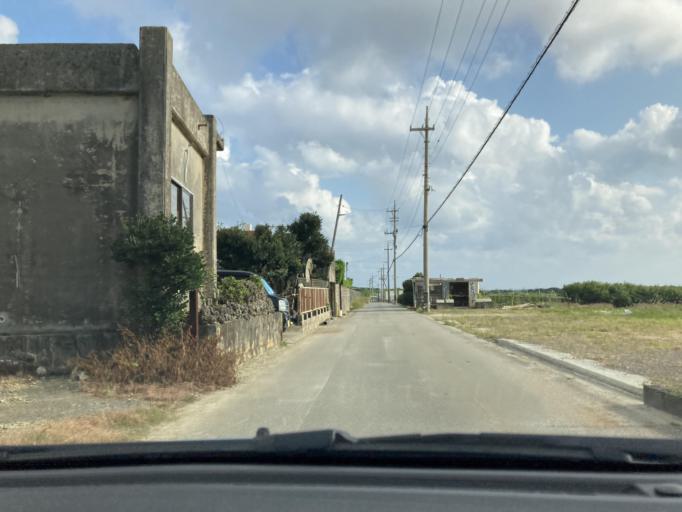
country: JP
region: Okinawa
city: Itoman
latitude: 26.0883
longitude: 127.6617
